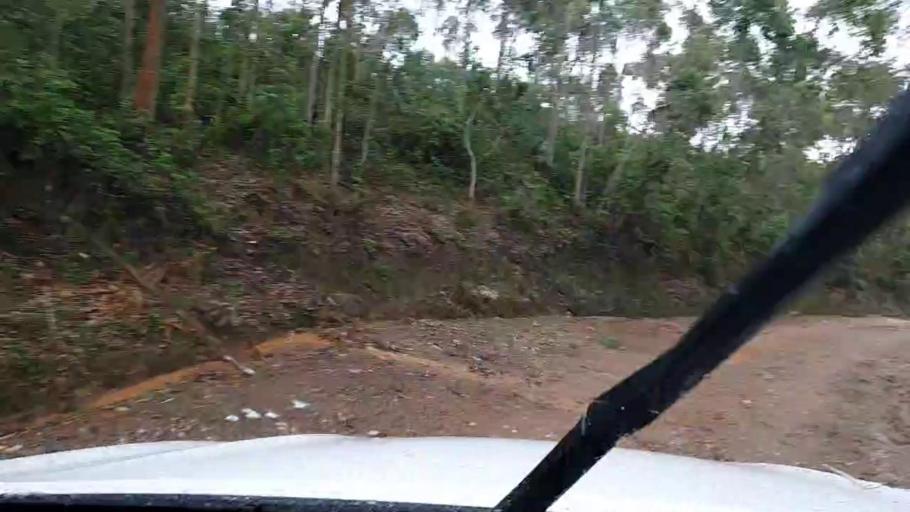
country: RW
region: Western Province
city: Cyangugu
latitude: -2.5493
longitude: 28.9786
